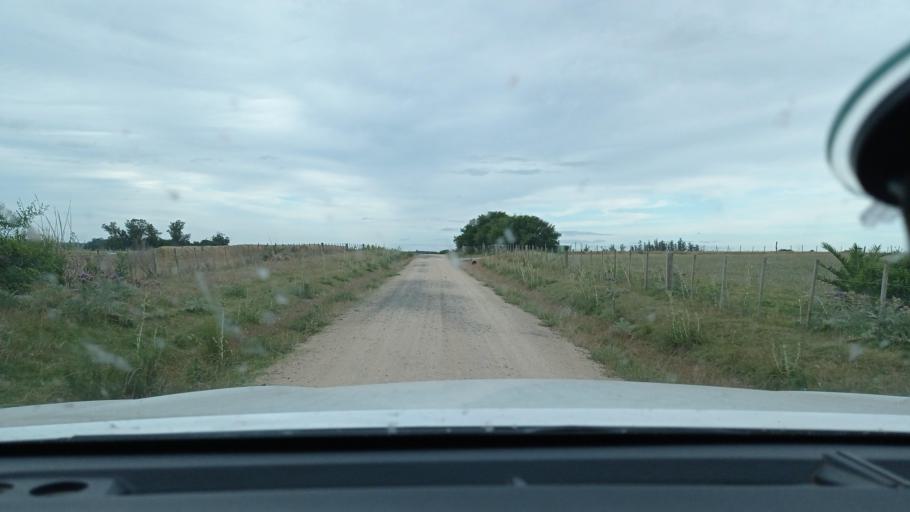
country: UY
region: Florida
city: Casupa
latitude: -34.1483
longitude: -55.7939
